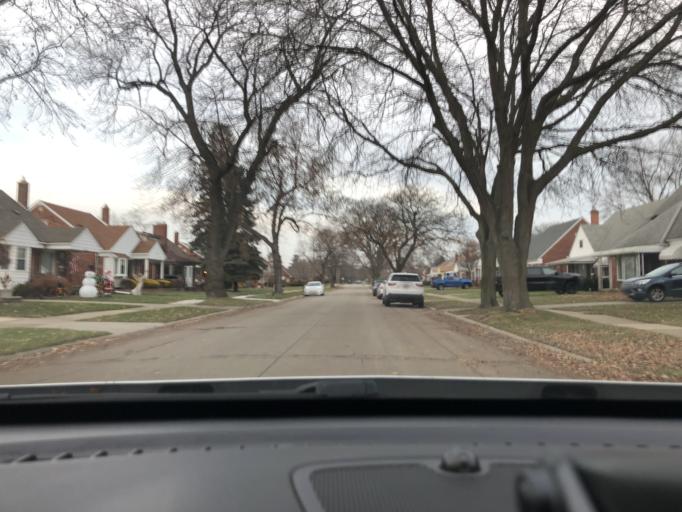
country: US
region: Michigan
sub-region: Wayne County
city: Allen Park
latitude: 42.2873
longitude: -83.2209
